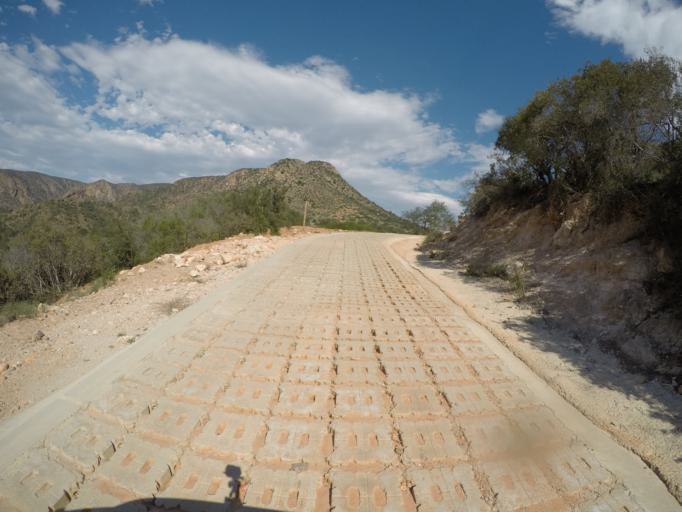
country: ZA
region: Eastern Cape
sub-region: Cacadu District Municipality
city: Kareedouw
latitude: -33.6547
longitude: 24.4178
